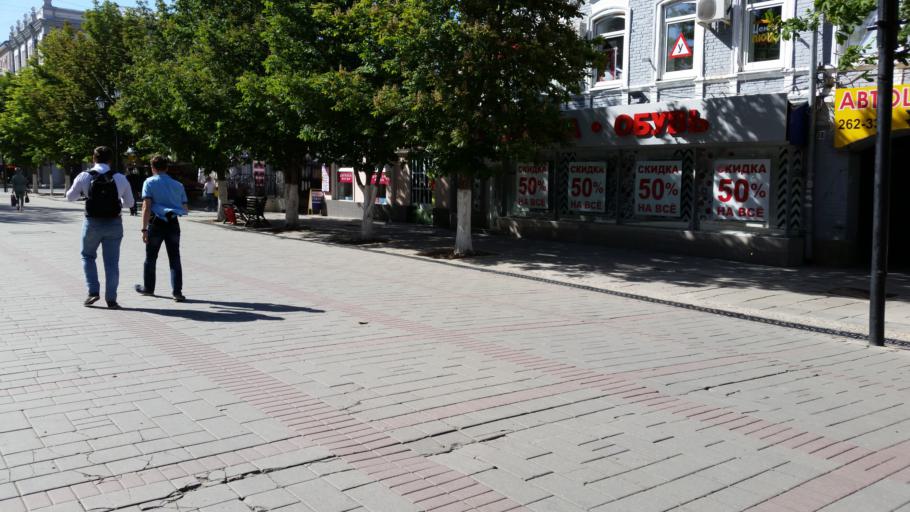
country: RU
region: Saratov
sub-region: Saratovskiy Rayon
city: Saratov
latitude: 51.5319
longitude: 46.0256
